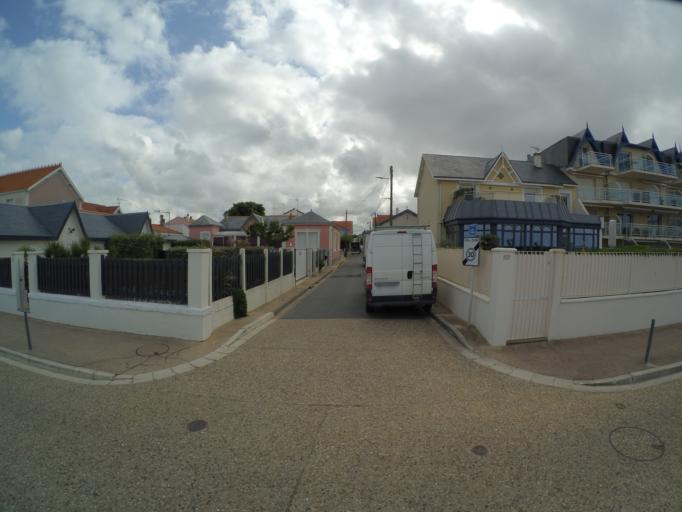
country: FR
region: Poitou-Charentes
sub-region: Departement de la Charente-Maritime
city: Chatelaillon-Plage
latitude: 46.0738
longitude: -1.0933
